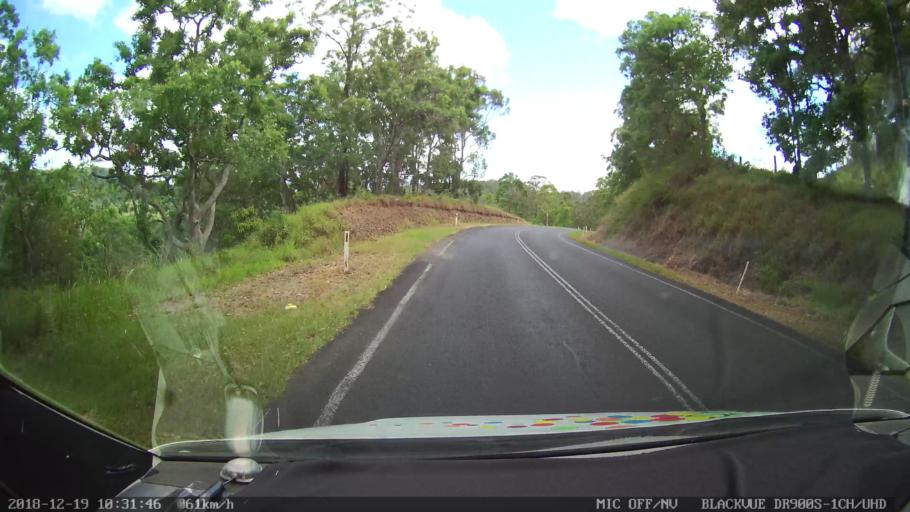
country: AU
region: New South Wales
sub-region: Lismore Municipality
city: Larnook
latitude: -28.5873
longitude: 153.1187
